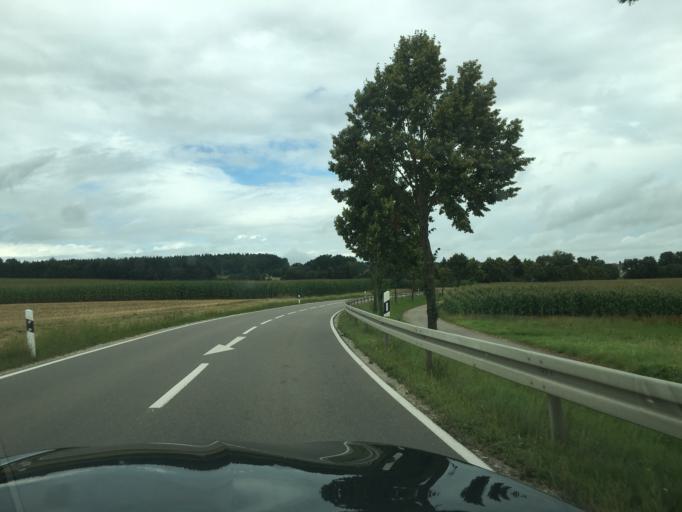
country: DE
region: Bavaria
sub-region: Swabia
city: Altenmunster
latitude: 48.4696
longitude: 10.5869
